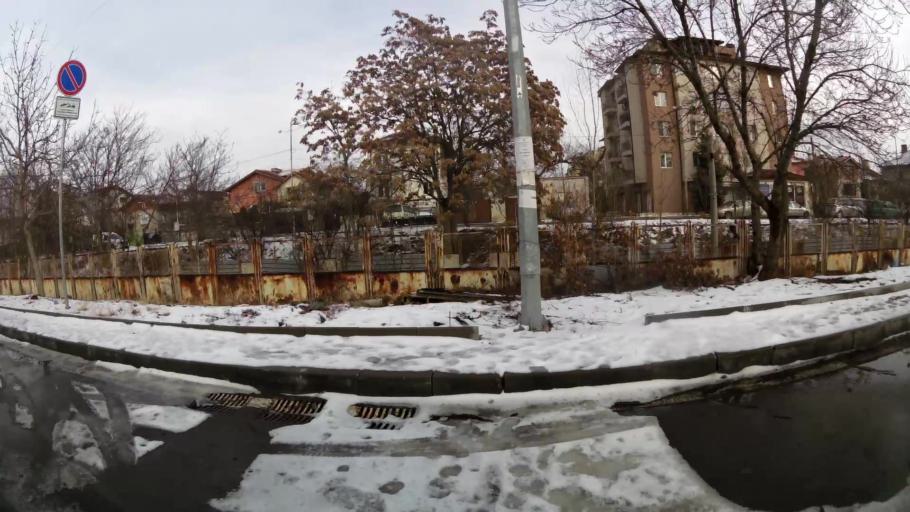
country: BG
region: Sofia-Capital
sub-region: Stolichna Obshtina
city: Sofia
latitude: 42.6987
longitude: 23.3785
